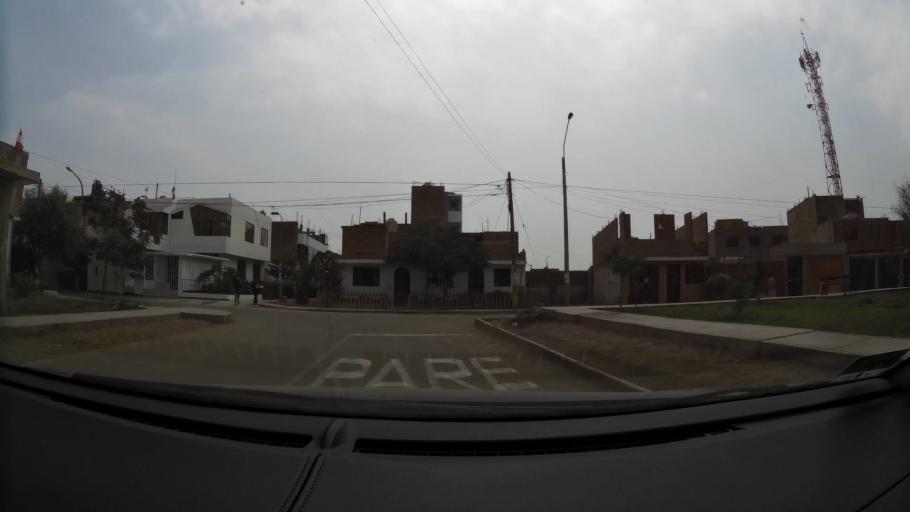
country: PE
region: Lima
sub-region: Lima
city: Santa Rosa
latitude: -11.7866
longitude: -77.1550
